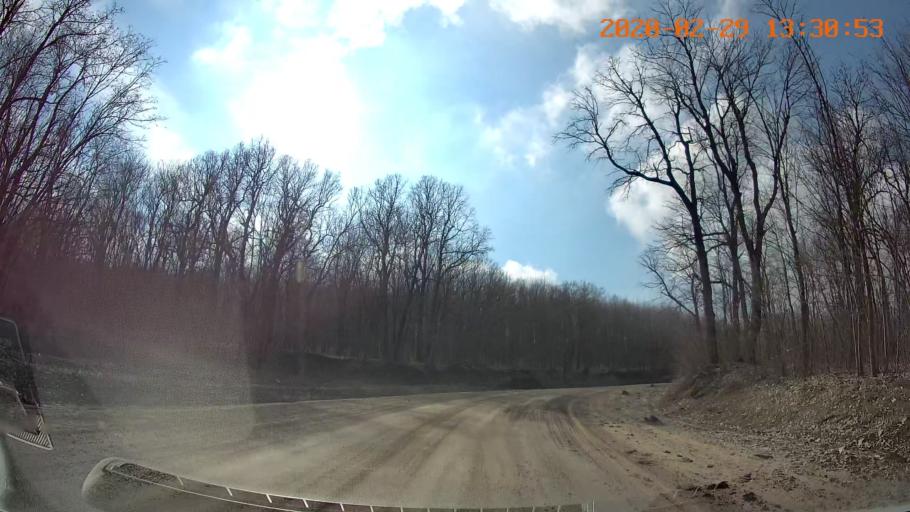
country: MD
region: Telenesti
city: Camenca
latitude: 47.8830
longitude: 28.6245
